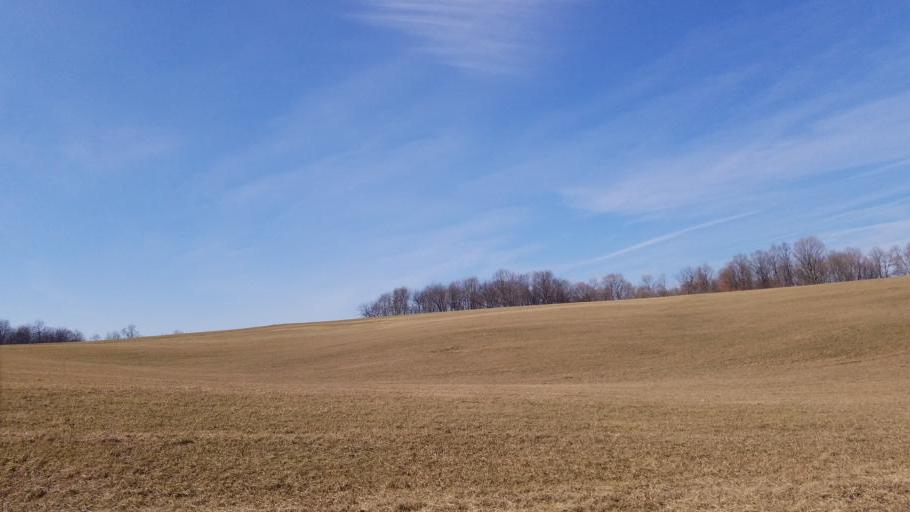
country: US
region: Ohio
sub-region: Knox County
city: Mount Vernon
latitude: 40.4820
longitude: -82.4352
